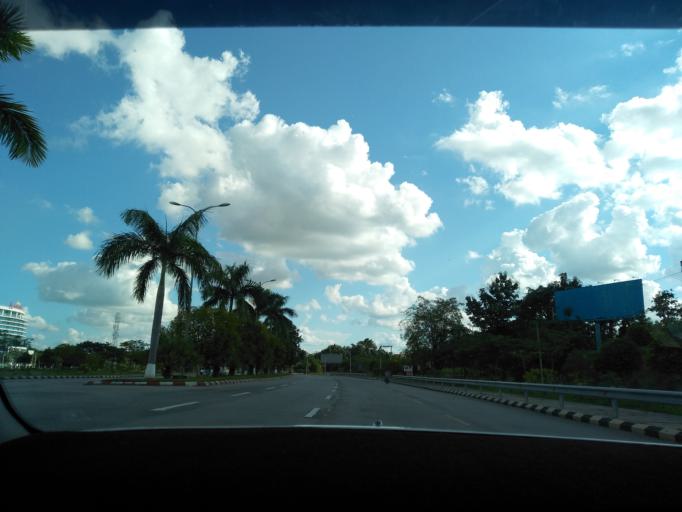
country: MM
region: Mandalay
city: Nay Pyi Taw
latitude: 19.7337
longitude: 96.1114
